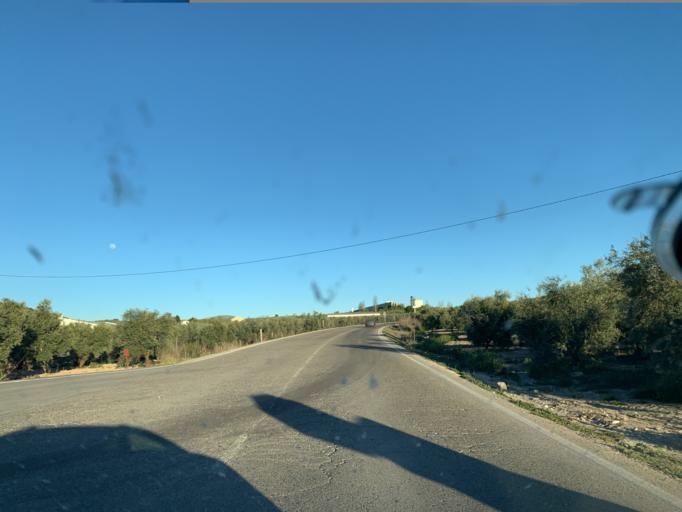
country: ES
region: Andalusia
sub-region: Provincia de Sevilla
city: Gilena
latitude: 37.2432
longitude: -4.9175
